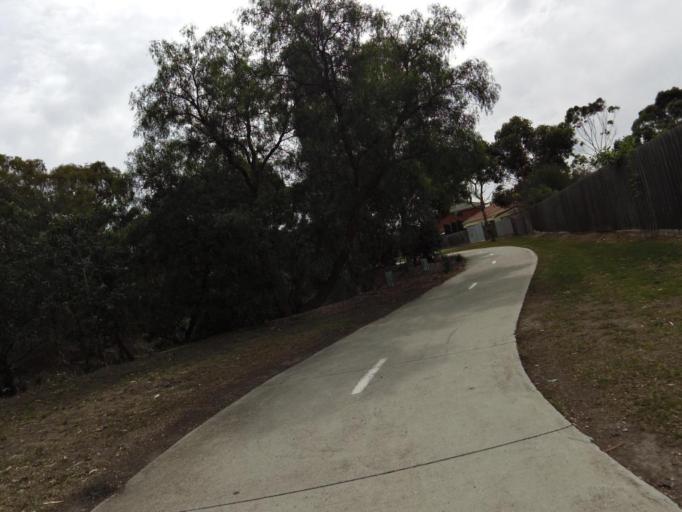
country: AU
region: Victoria
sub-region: Hume
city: Sunbury
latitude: -37.5708
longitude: 144.7133
